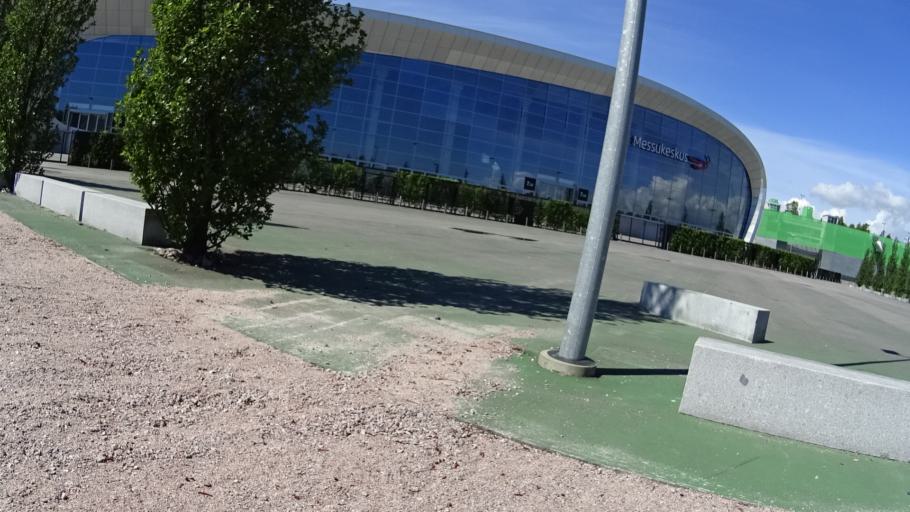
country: FI
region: Uusimaa
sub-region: Helsinki
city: Helsinki
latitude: 60.2039
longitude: 24.9402
